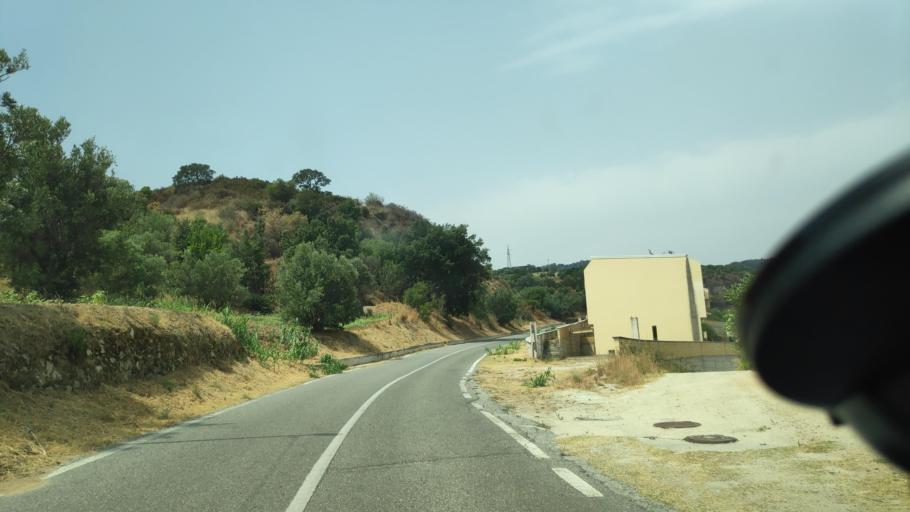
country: IT
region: Calabria
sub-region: Provincia di Catanzaro
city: Marina di Davoli
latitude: 38.6449
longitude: 16.5351
